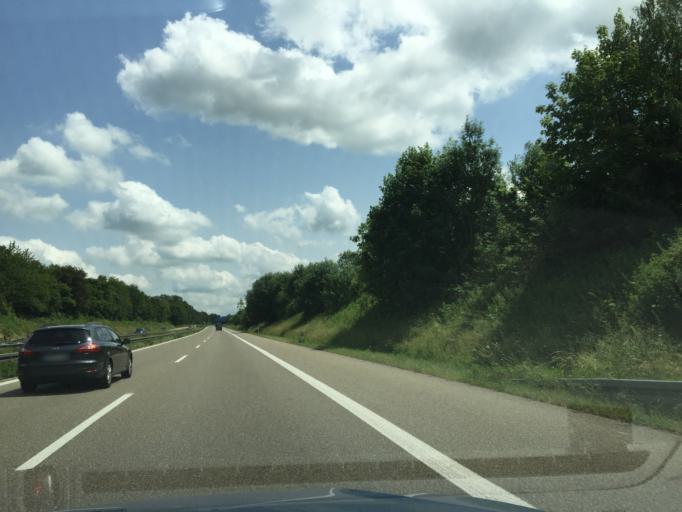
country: DE
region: Bavaria
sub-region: Swabia
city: Senden
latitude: 48.3317
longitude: 10.0573
